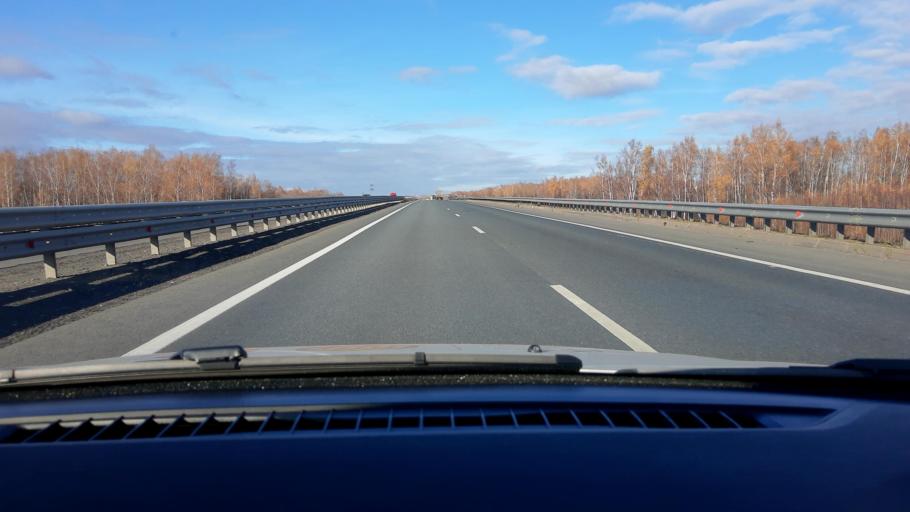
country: RU
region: Nizjnij Novgorod
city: Burevestnik
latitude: 56.1309
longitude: 43.7791
